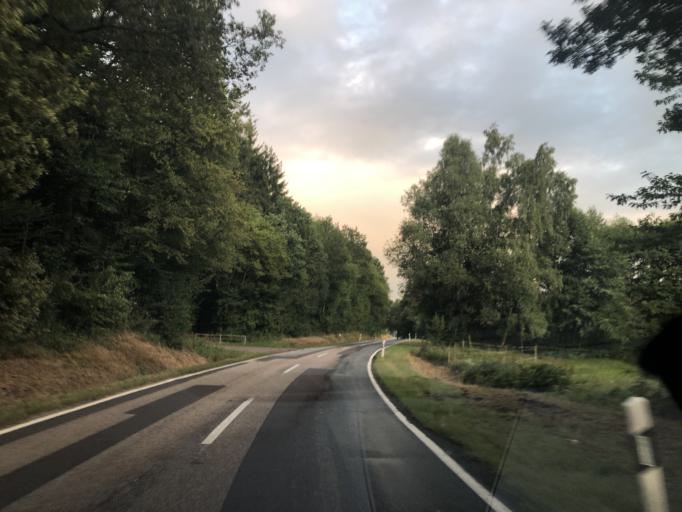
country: DE
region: Rheinland-Pfalz
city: Grimburg
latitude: 49.5890
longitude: 6.8816
